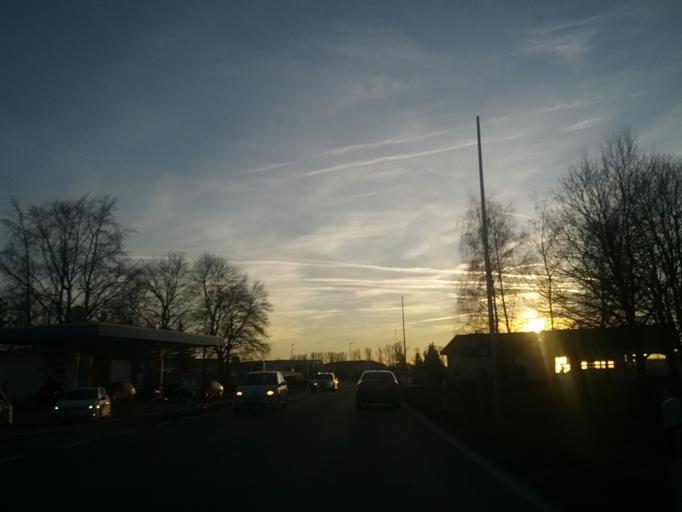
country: DE
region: Bavaria
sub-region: Swabia
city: Heimertingen
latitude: 48.0355
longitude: 10.1539
